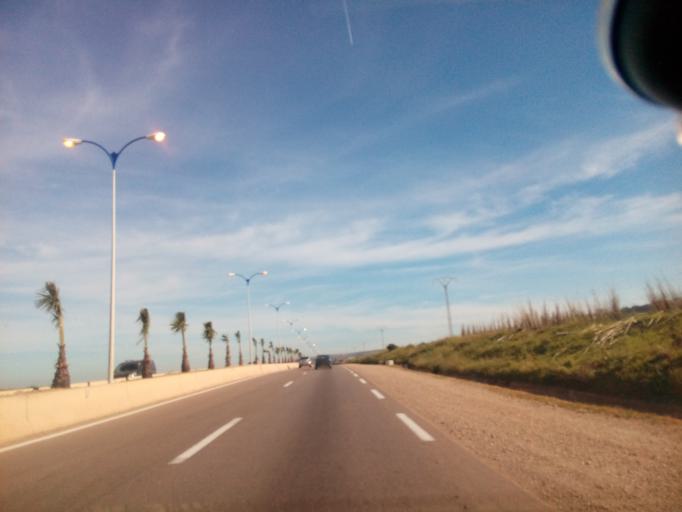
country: DZ
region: Mostaganem
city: Mostaganem
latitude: 35.8175
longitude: -0.0234
